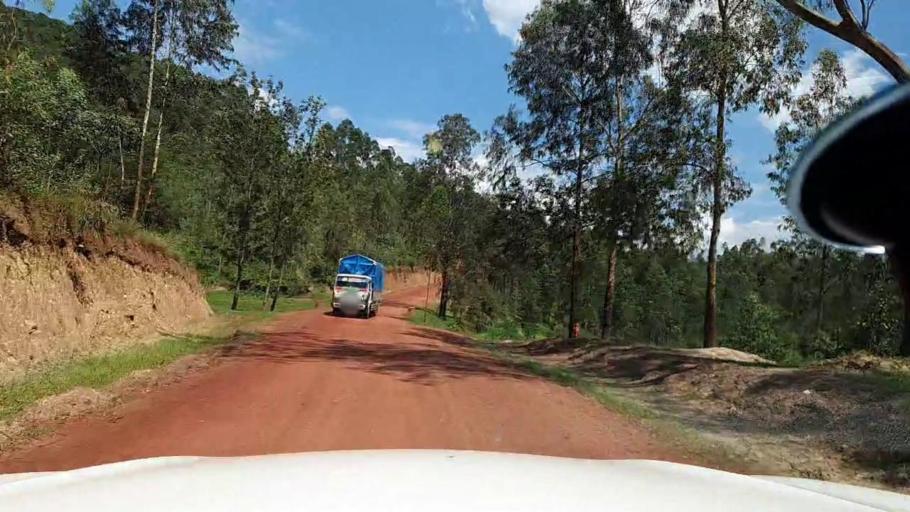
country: RW
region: Kigali
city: Kigali
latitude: -1.7688
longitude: 29.8739
